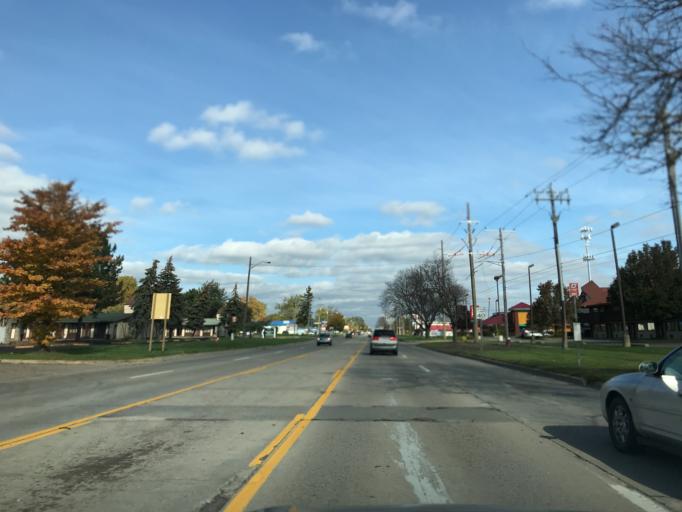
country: US
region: Michigan
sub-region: Oakland County
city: Madison Heights
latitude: 42.4856
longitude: -83.0848
